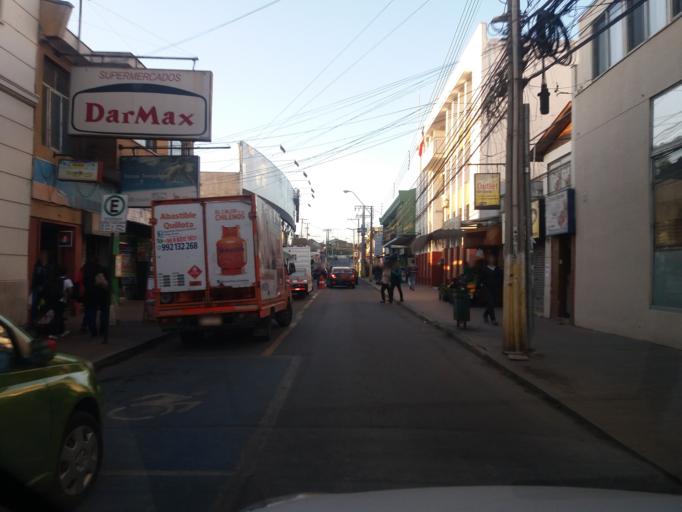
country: CL
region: Valparaiso
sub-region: Provincia de Quillota
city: Quillota
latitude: -32.8780
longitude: -71.2466
